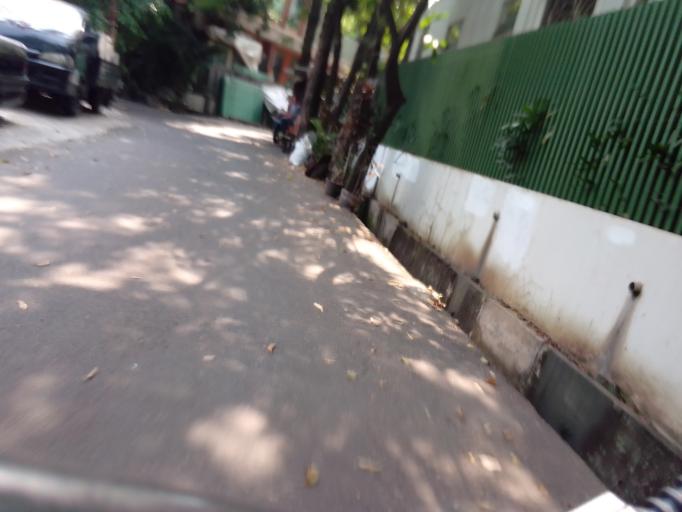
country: ID
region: Jakarta Raya
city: Jakarta
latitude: -6.2086
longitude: 106.8092
